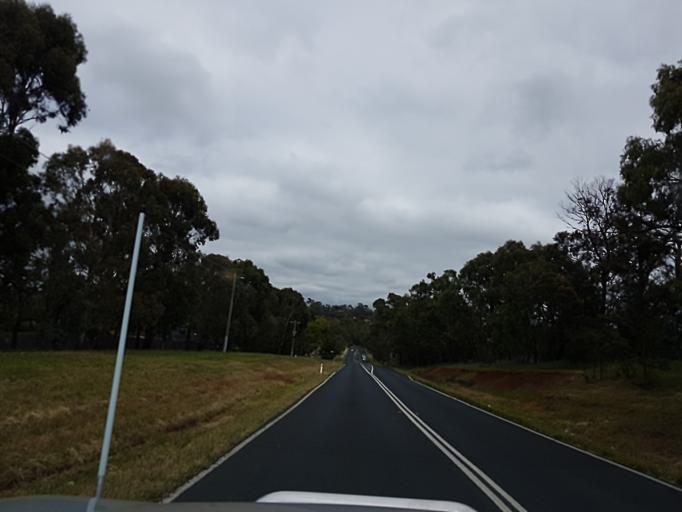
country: AU
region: Victoria
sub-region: Yarra Ranges
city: Lilydale
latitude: -37.7755
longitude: 145.3368
